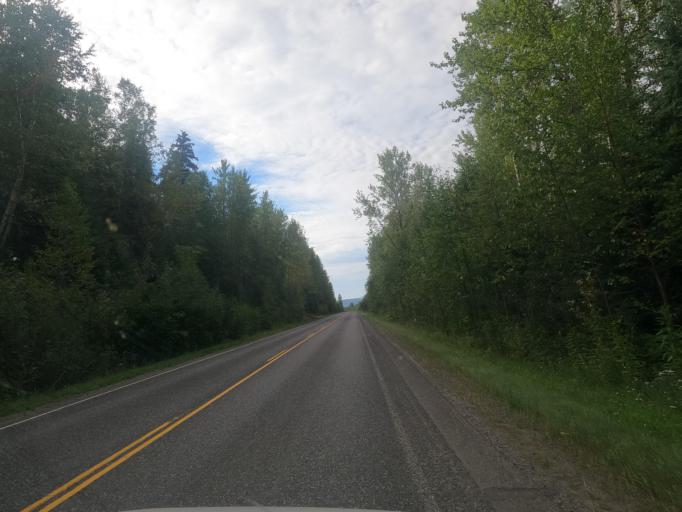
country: CA
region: British Columbia
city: Terrace
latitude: 55.3217
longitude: -128.0901
